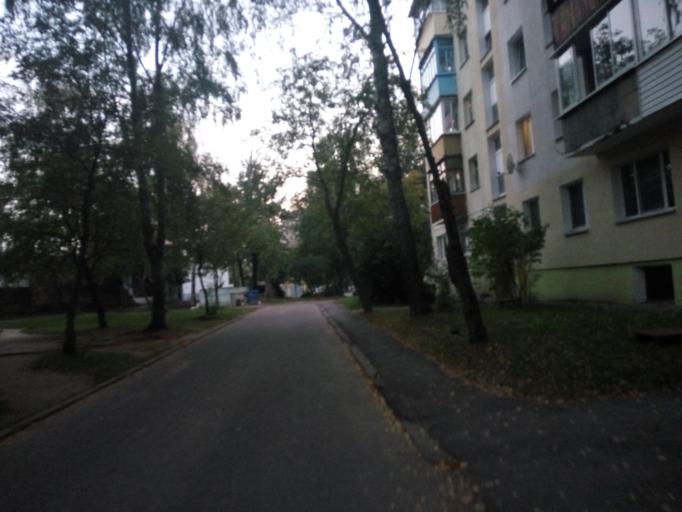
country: BY
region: Vitebsk
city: Vitebsk
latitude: 55.2014
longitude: 30.2420
